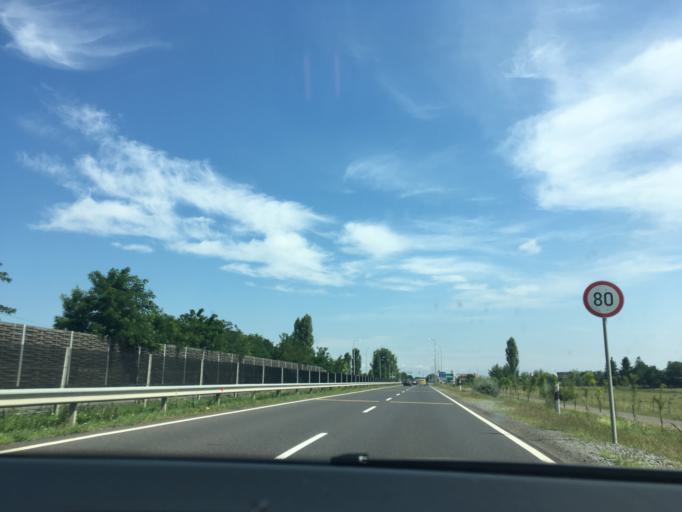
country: HU
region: Szabolcs-Szatmar-Bereg
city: Nyiregyhaza
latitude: 47.8984
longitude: 21.7111
